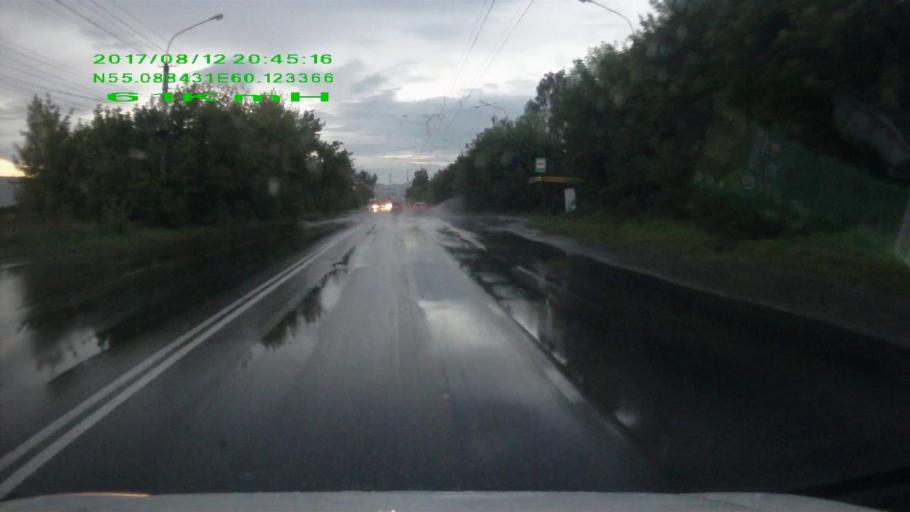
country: RU
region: Chelyabinsk
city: Miass
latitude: 55.0886
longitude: 60.1235
